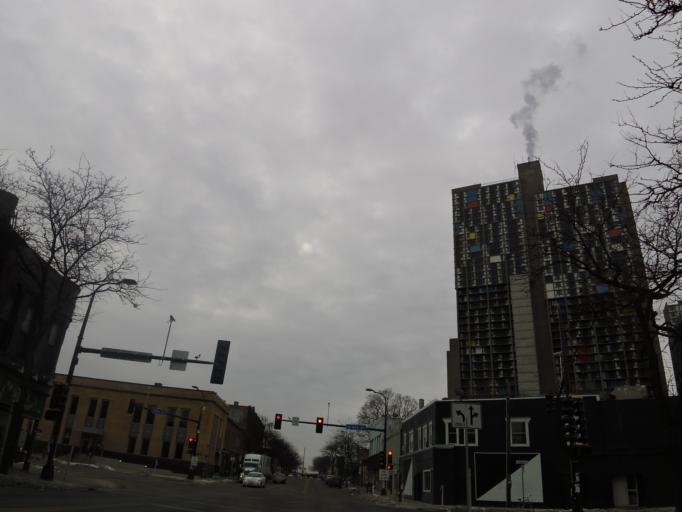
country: US
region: Minnesota
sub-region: Hennepin County
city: Minneapolis
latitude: 44.9705
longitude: -93.2473
